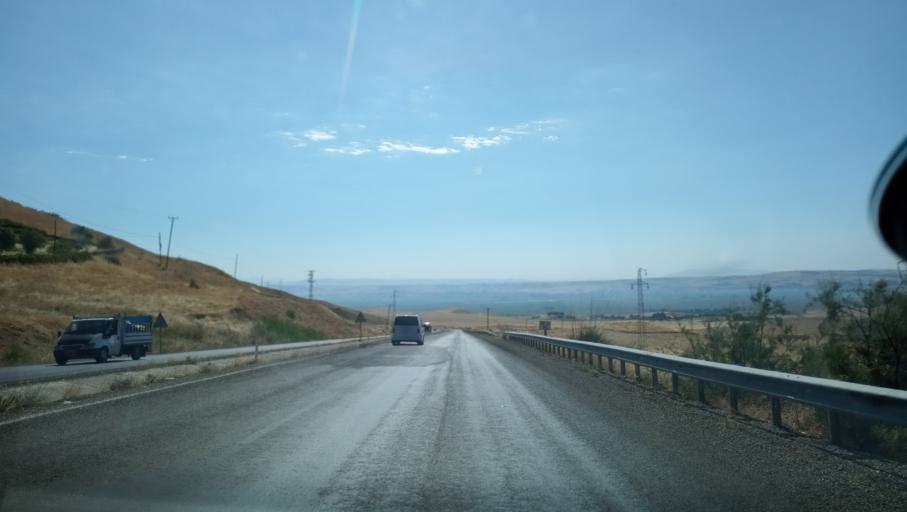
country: TR
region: Diyarbakir
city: Malabadi
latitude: 38.1189
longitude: 41.1313
